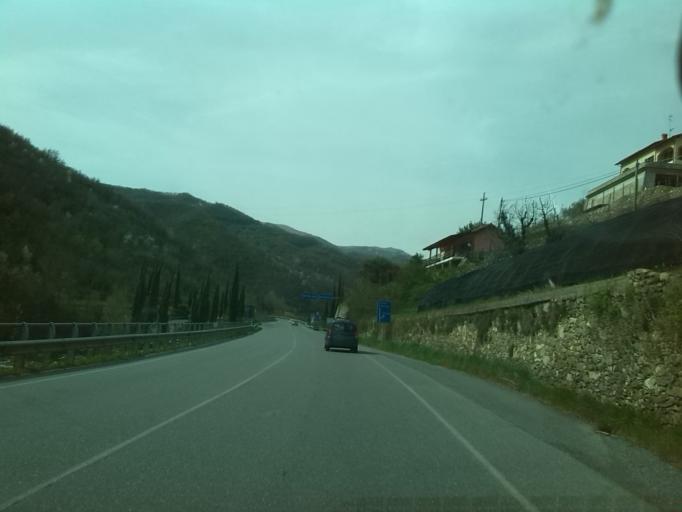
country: IT
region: Liguria
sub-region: Provincia di Imperia
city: Vessalico
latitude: 44.0492
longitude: 7.9671
